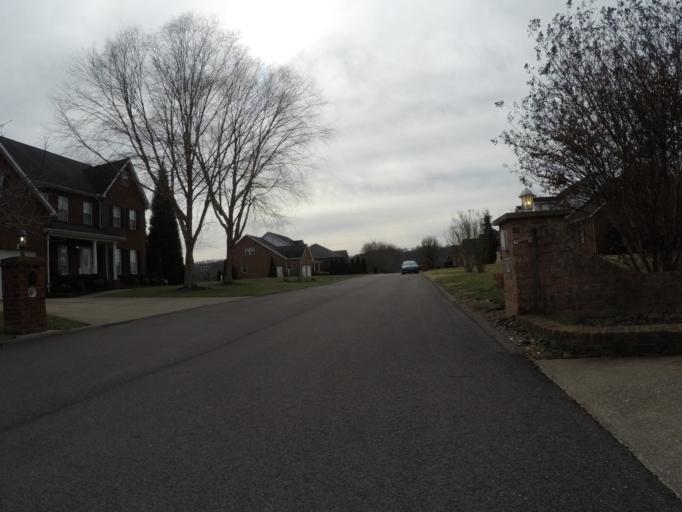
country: US
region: West Virginia
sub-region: Cabell County
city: Pea Ridge
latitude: 38.4494
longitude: -82.3484
